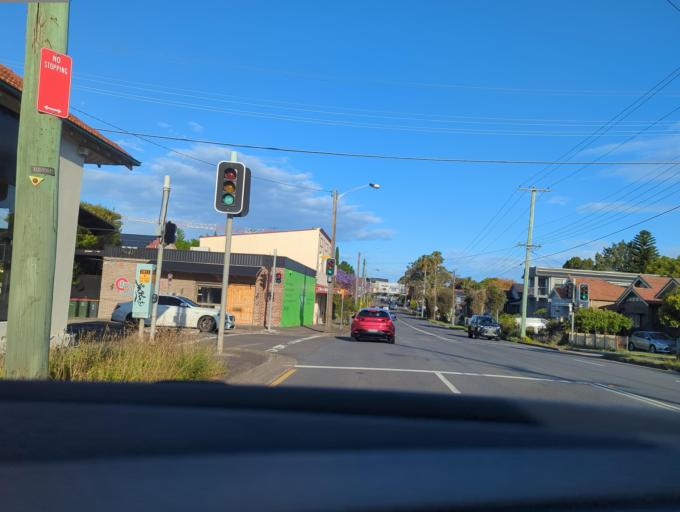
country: AU
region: New South Wales
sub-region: Rockdale
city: Bexley
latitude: -33.9498
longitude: 151.1229
